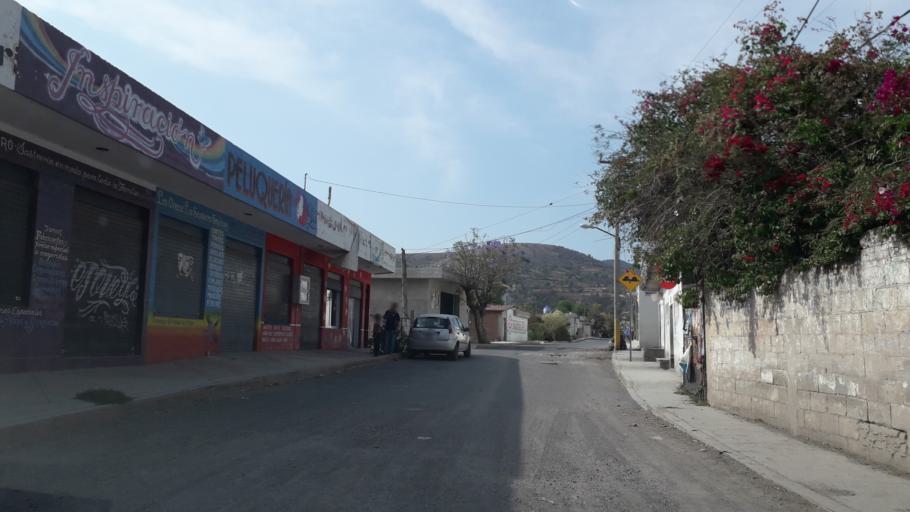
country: MX
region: Puebla
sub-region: Puebla
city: San Andres Azumiatla
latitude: 18.8990
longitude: -98.2564
